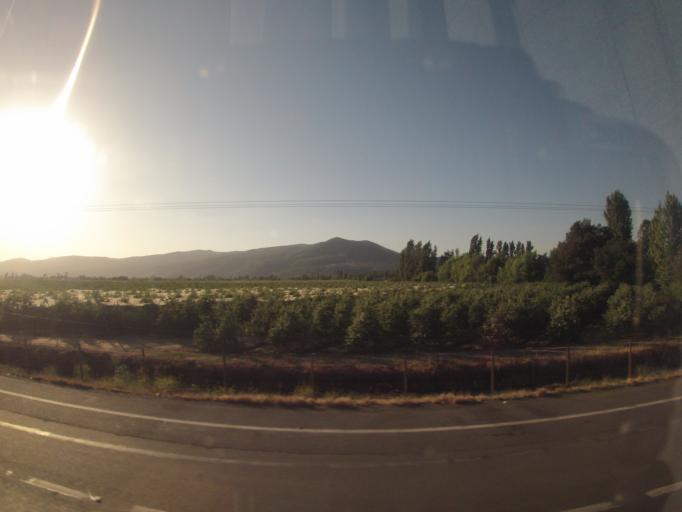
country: CL
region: O'Higgins
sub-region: Provincia de Colchagua
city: Chimbarongo
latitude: -34.6983
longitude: -71.0208
